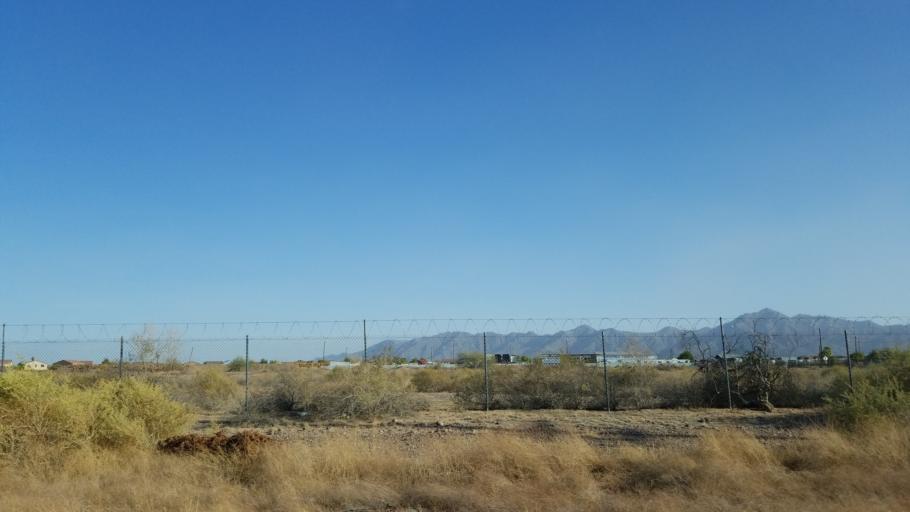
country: US
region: Arizona
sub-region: Maricopa County
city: Laveen
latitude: 33.3919
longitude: -112.2191
